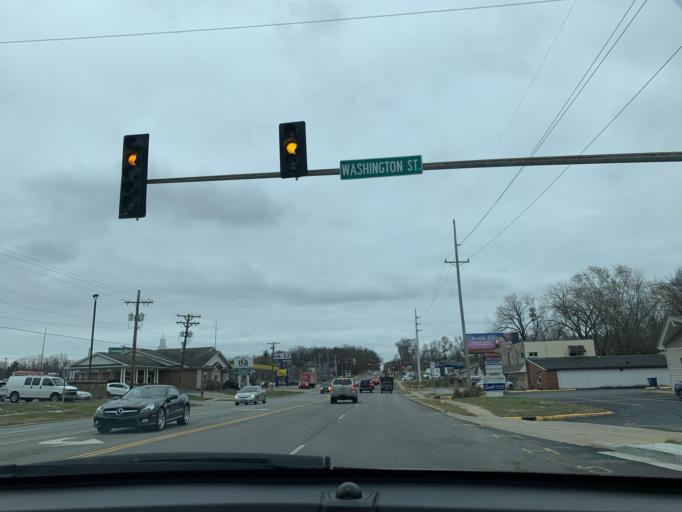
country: US
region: Illinois
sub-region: Sangamon County
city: Leland Grove
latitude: 39.8013
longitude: -89.6872
